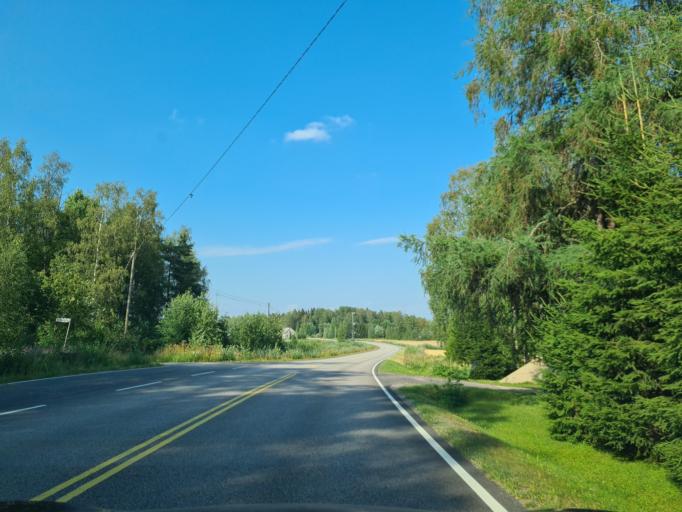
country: FI
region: Satakunta
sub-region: Pohjois-Satakunta
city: Karvia
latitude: 62.2081
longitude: 22.6015
